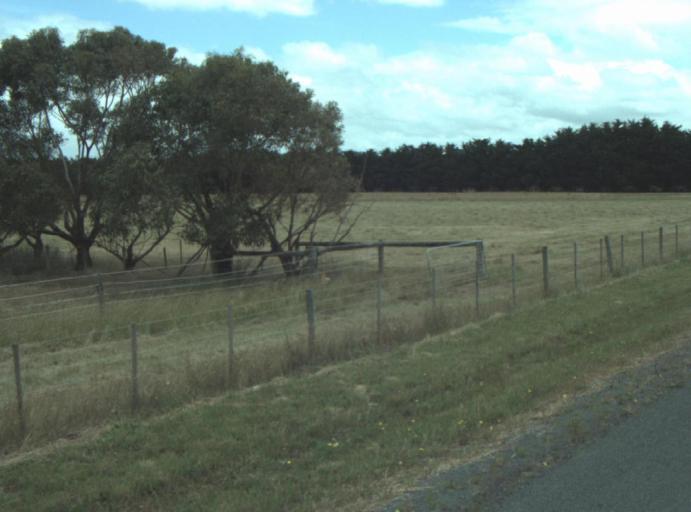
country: AU
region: Victoria
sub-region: Greater Geelong
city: Wandana Heights
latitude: -38.2458
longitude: 144.3067
